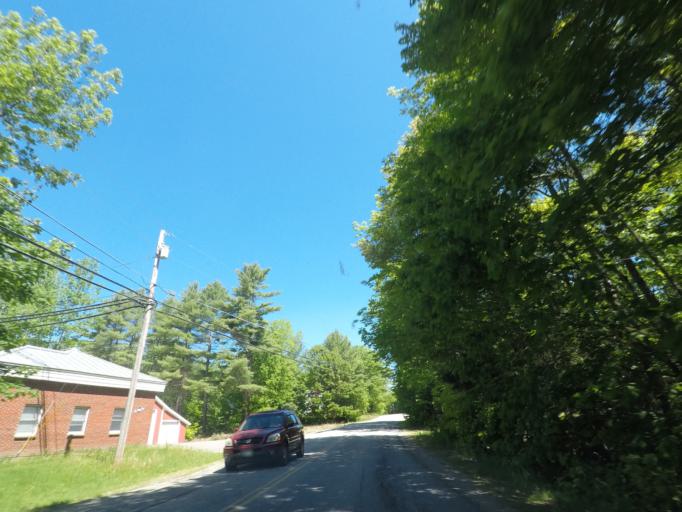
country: US
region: Maine
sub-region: Kennebec County
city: Manchester
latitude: 44.2500
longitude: -69.8998
